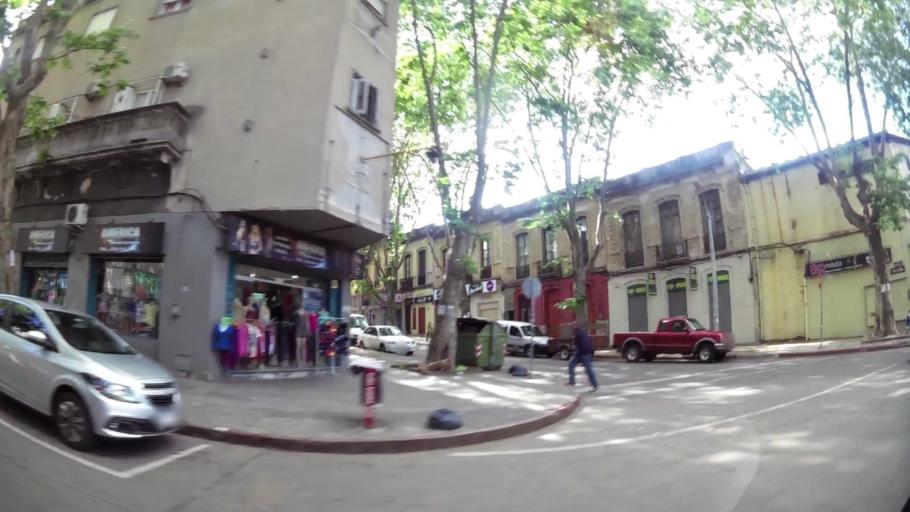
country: UY
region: Montevideo
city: Montevideo
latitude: -34.8837
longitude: -56.1785
